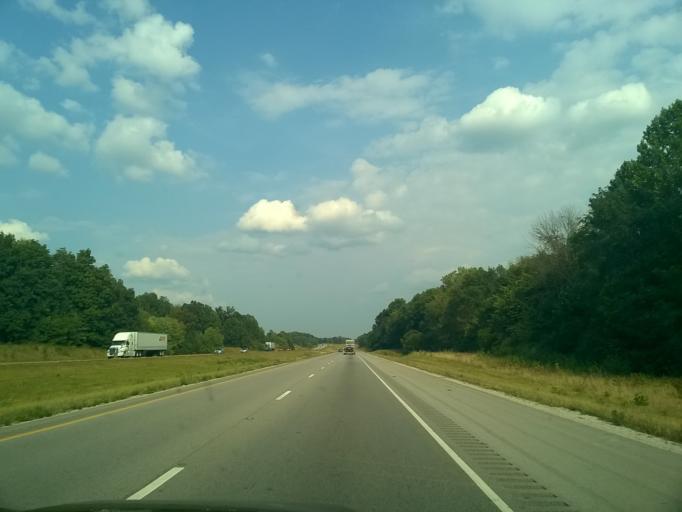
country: US
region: Indiana
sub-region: Vigo County
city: Seelyville
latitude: 39.4457
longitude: -87.2255
